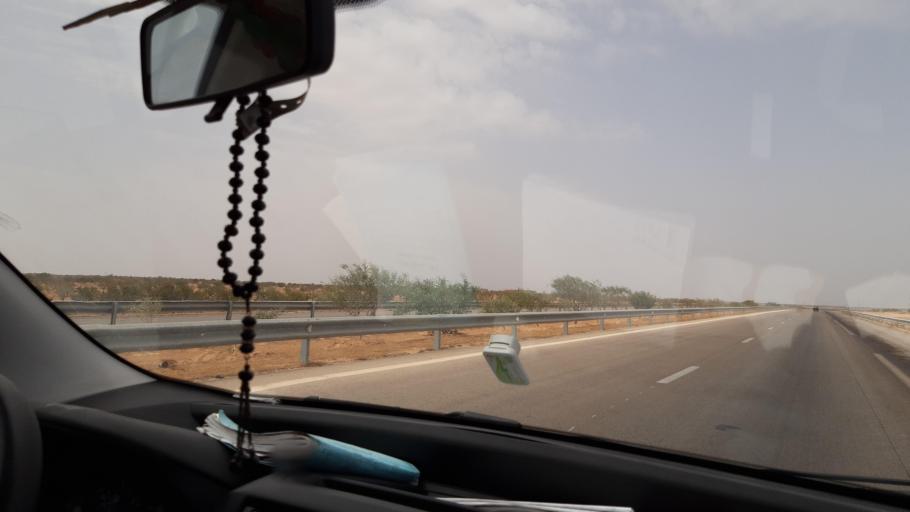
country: TN
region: Safaqis
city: Sfax
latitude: 34.8594
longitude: 10.6853
